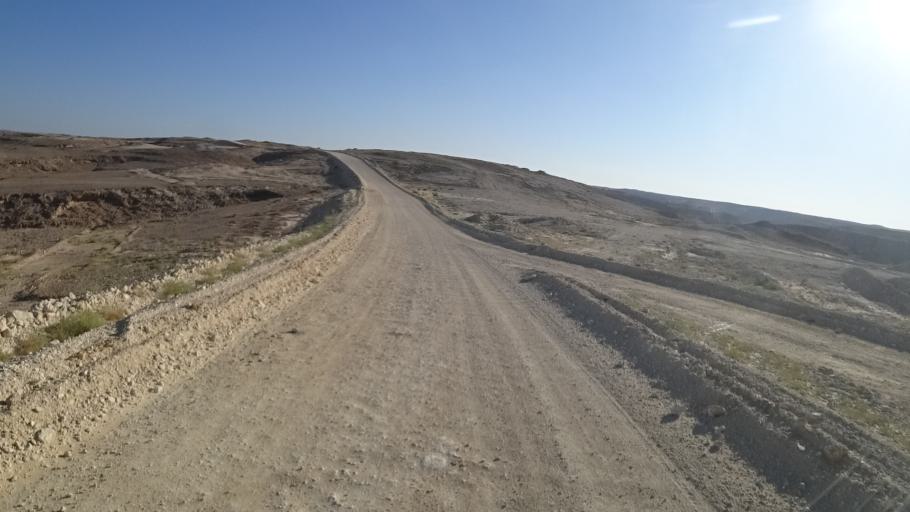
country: YE
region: Al Mahrah
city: Hawf
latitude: 17.2381
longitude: 53.3194
